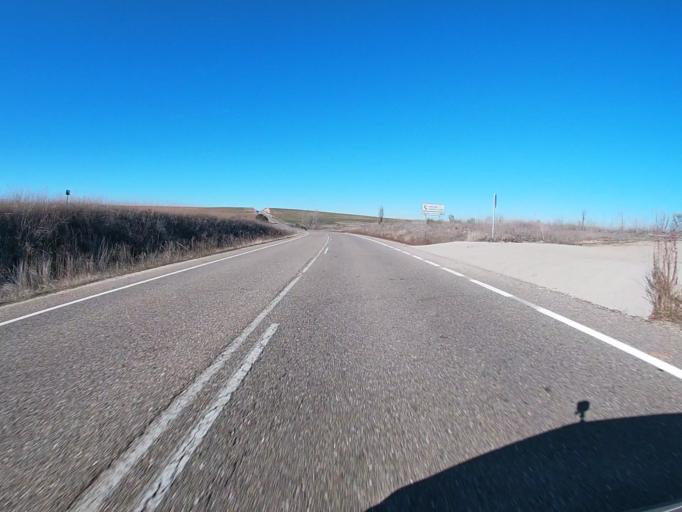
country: ES
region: Castille and Leon
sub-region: Provincia de Salamanca
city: Almenara de Tormes
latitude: 41.0671
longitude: -5.8258
